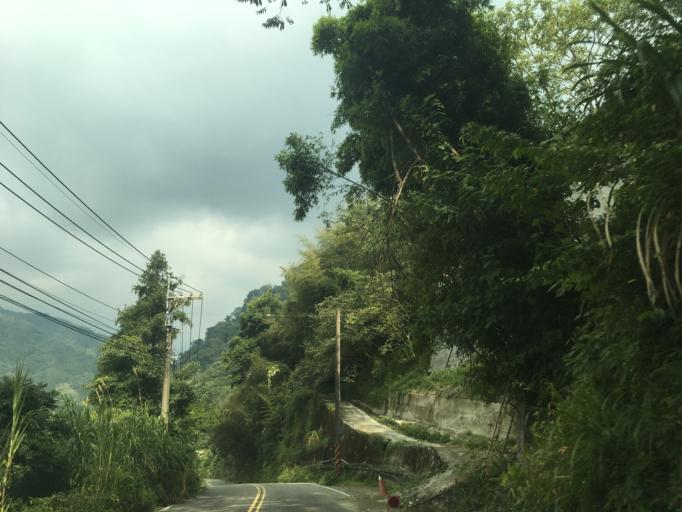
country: TW
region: Taiwan
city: Fengyuan
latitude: 24.3352
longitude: 120.9303
